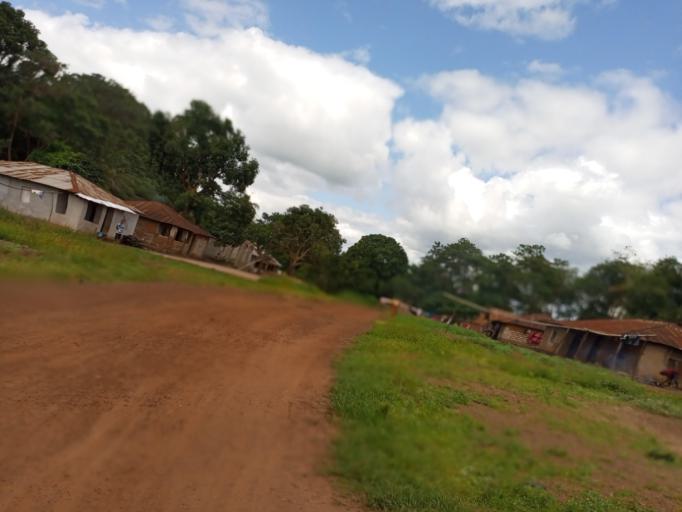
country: SL
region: Northern Province
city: Kamakwie
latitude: 9.5077
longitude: -12.2243
